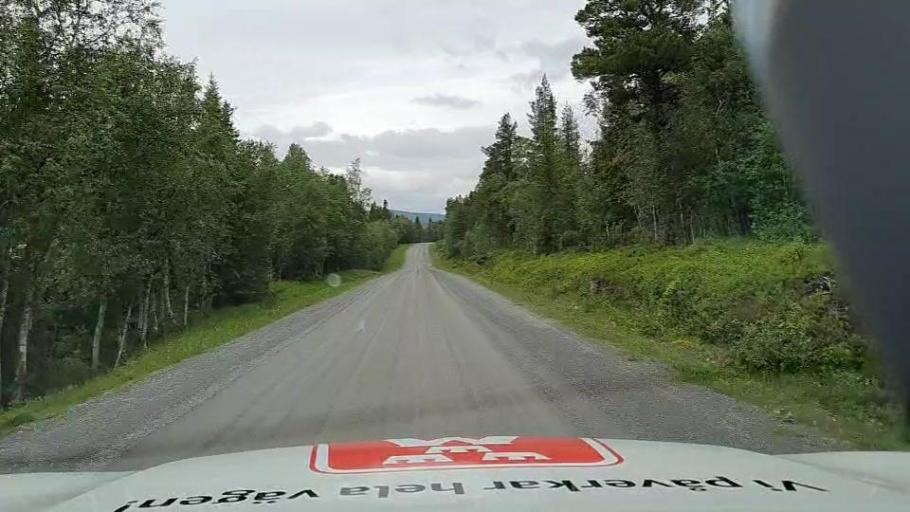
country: NO
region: Nord-Trondelag
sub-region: Snasa
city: Snaase
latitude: 63.7351
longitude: 12.5052
